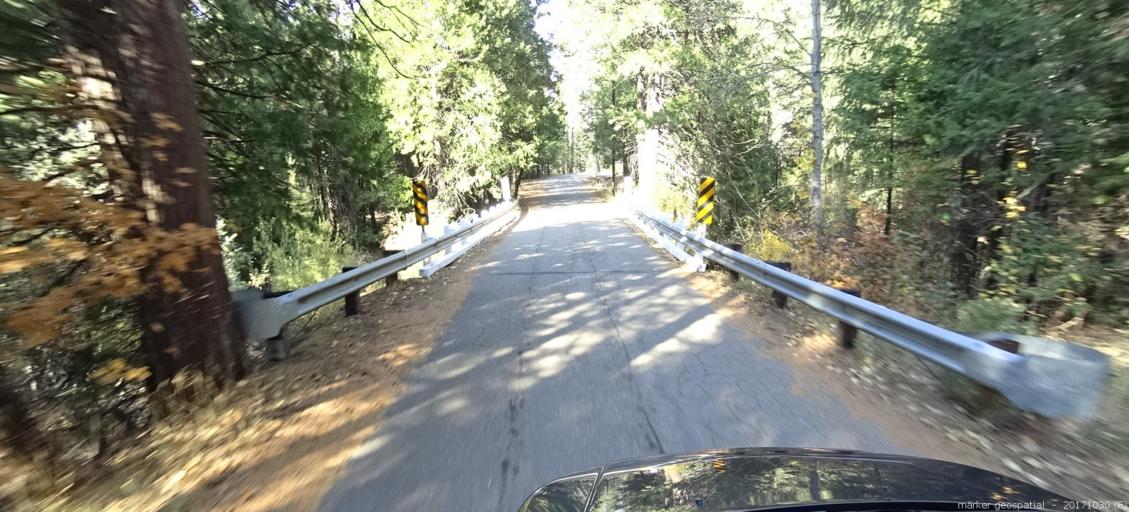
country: US
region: California
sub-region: Shasta County
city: Shingletown
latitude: 40.5102
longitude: -121.7278
